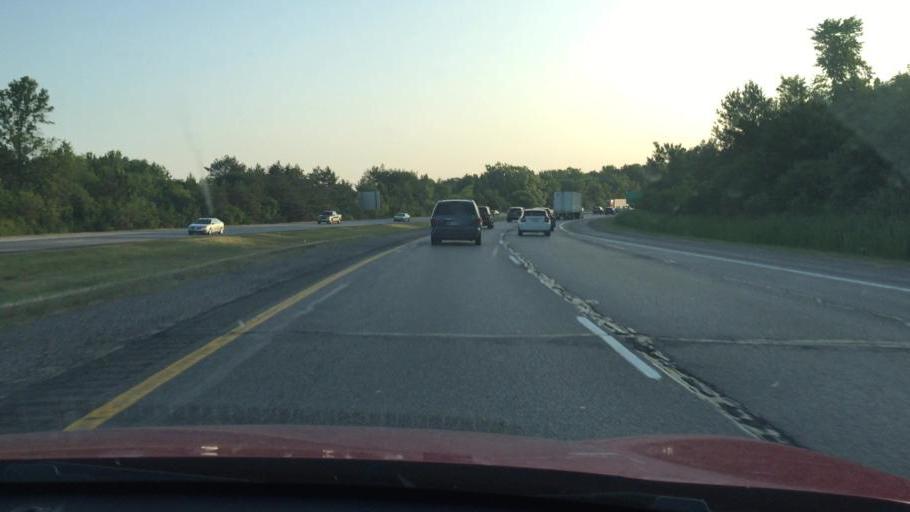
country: US
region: Michigan
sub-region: Washtenaw County
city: Ann Arbor
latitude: 42.2592
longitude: -83.6825
